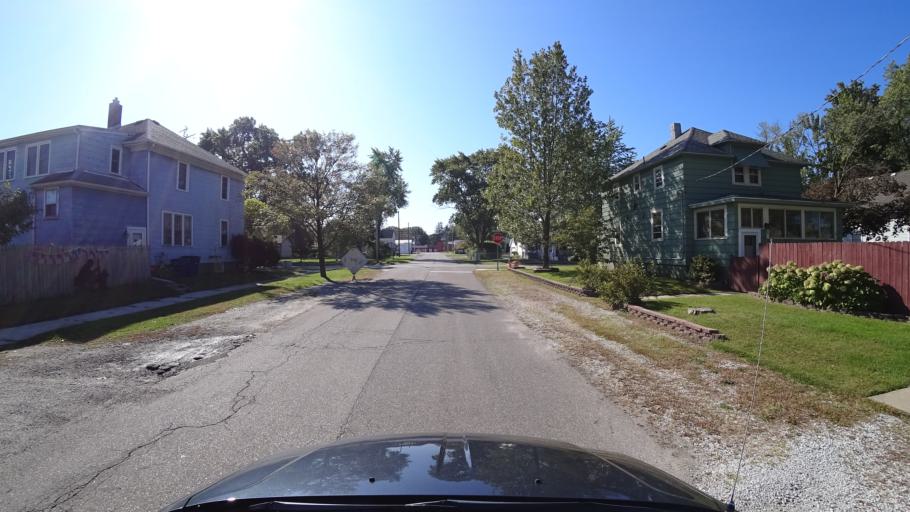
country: US
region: Indiana
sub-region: LaPorte County
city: Michigan City
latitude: 41.7028
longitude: -86.8921
